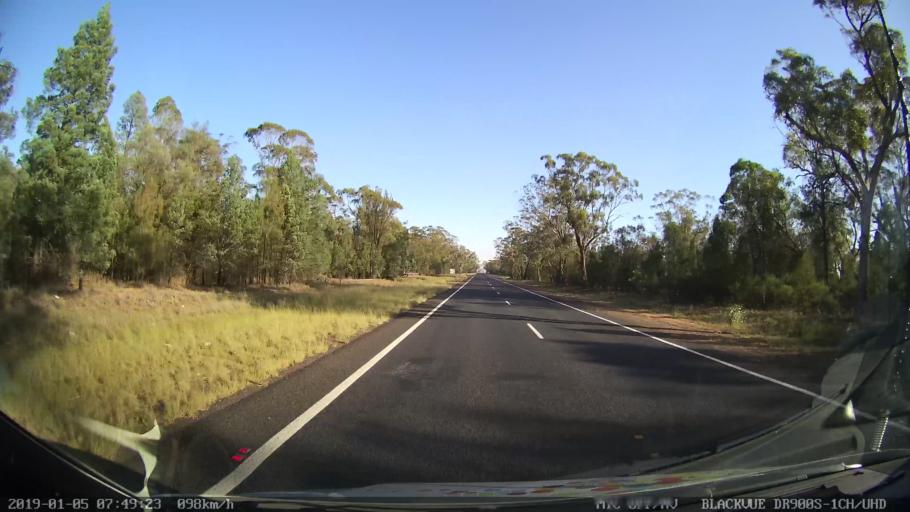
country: AU
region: New South Wales
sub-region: Gilgandra
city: Gilgandra
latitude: -31.8026
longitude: 148.6364
